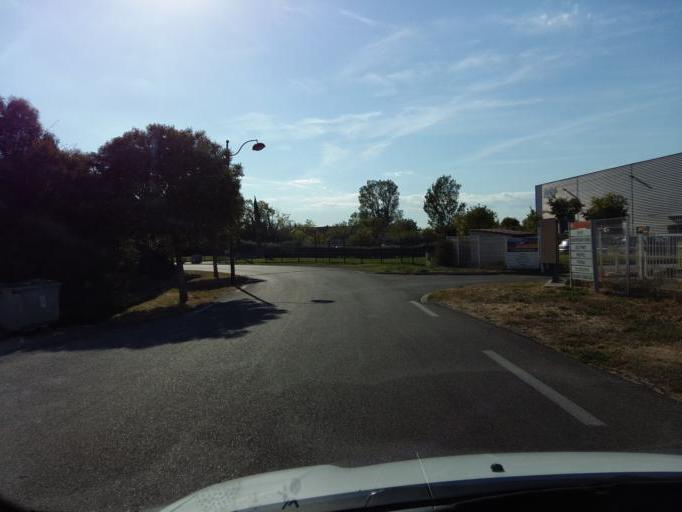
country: FR
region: Provence-Alpes-Cote d'Azur
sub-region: Departement du Vaucluse
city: Le Thor
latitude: 43.9238
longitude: 5.0184
